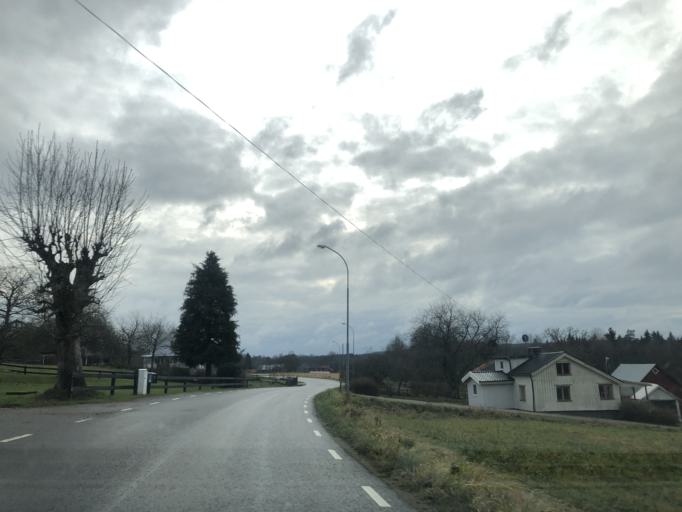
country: SE
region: Vaestra Goetaland
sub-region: Ulricehamns Kommun
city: Ulricehamn
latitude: 57.8171
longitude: 13.2446
